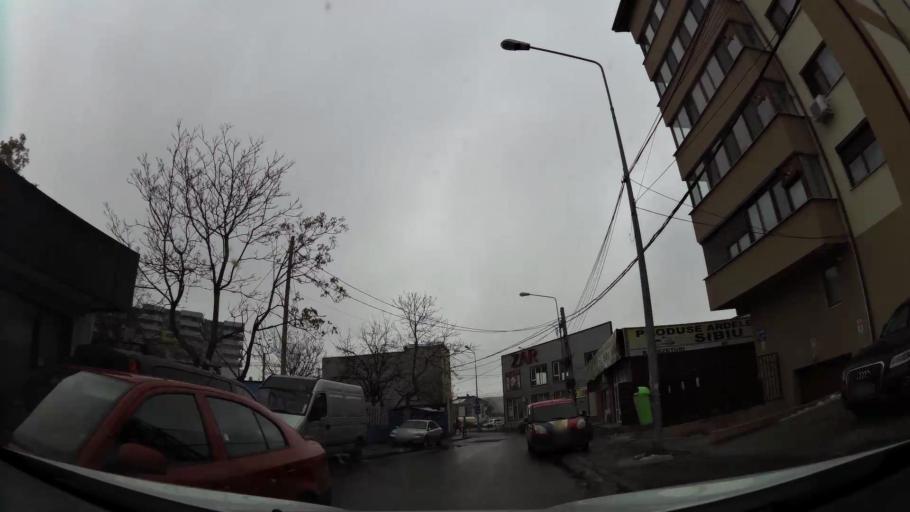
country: RO
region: Bucuresti
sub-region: Municipiul Bucuresti
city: Bucharest
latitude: 44.4122
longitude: 26.1269
